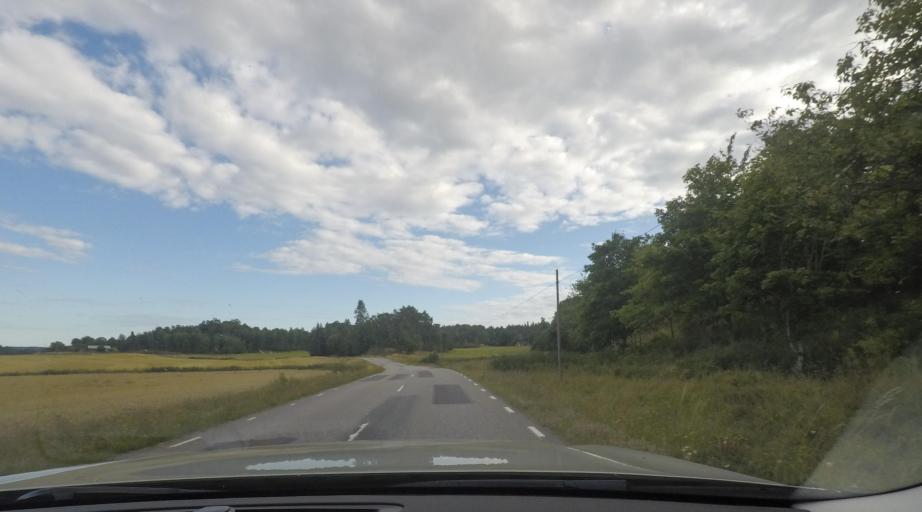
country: SE
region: Soedermanland
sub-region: Trosa Kommun
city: Trosa
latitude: 58.9892
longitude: 17.6770
